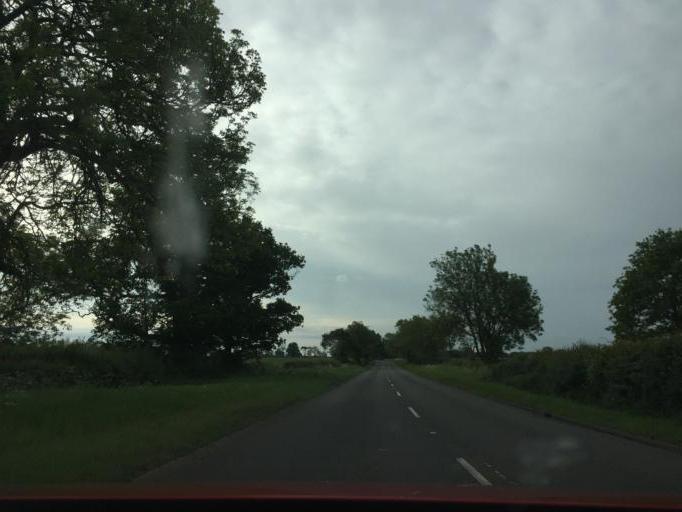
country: GB
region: England
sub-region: Leicestershire
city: Hinckley
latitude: 52.4823
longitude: -1.3350
